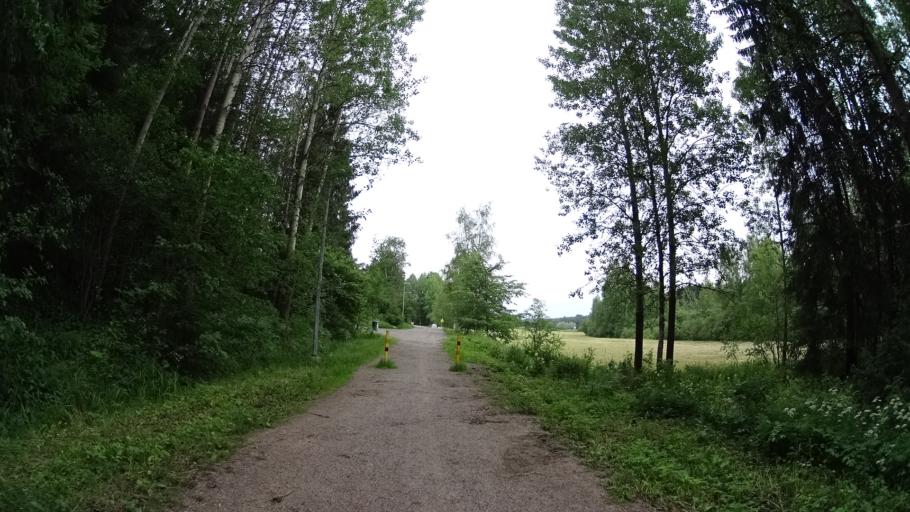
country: FI
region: Uusimaa
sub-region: Helsinki
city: Kilo
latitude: 60.2825
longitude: 24.7874
